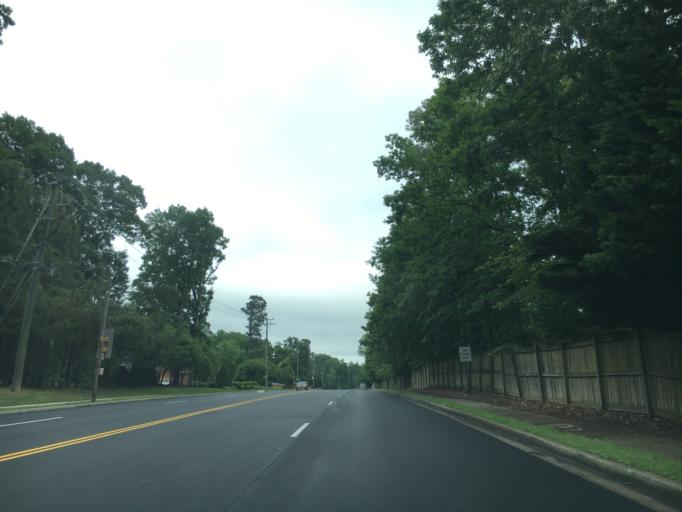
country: US
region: Virginia
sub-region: Henrico County
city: Short Pump
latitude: 37.6350
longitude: -77.6303
